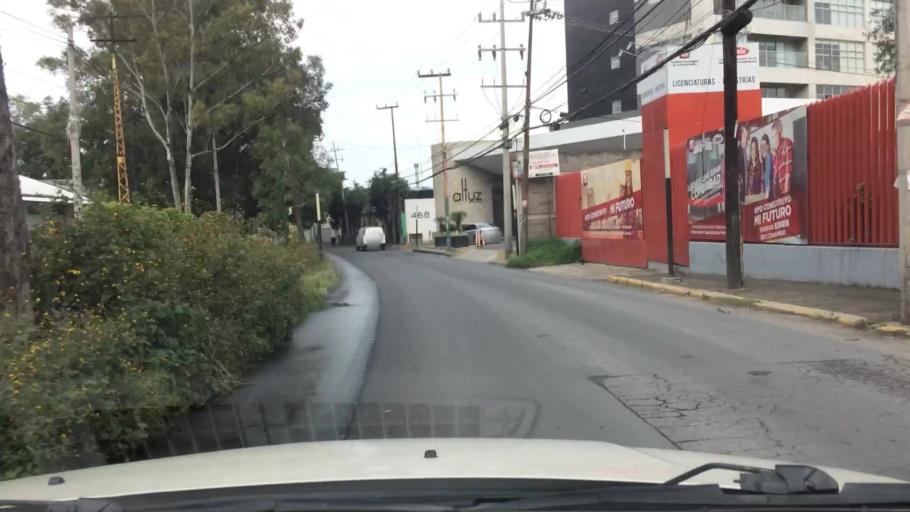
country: MX
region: Mexico City
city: Magdalena Contreras
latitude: 19.3380
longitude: -99.2119
